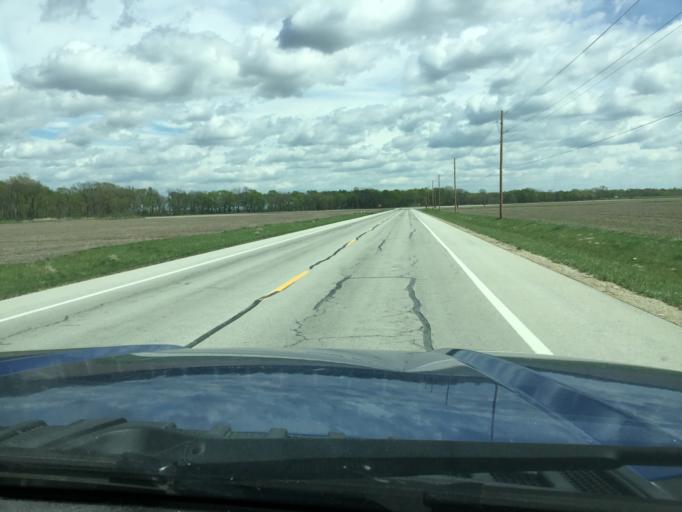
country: US
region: Kansas
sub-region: Douglas County
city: Lawrence
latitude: 38.9136
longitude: -95.2735
